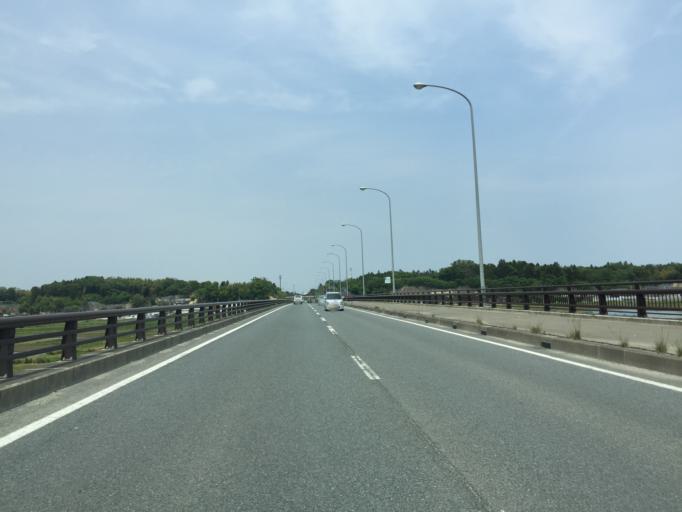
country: JP
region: Miyagi
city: Marumori
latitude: 37.8040
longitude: 140.9436
